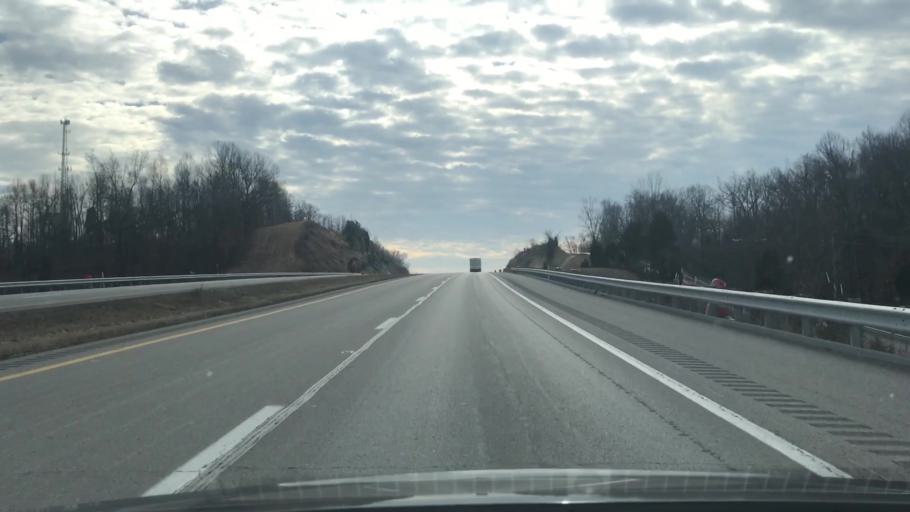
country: US
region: Kentucky
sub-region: Ohio County
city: Hartford
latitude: 37.5290
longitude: -86.9219
